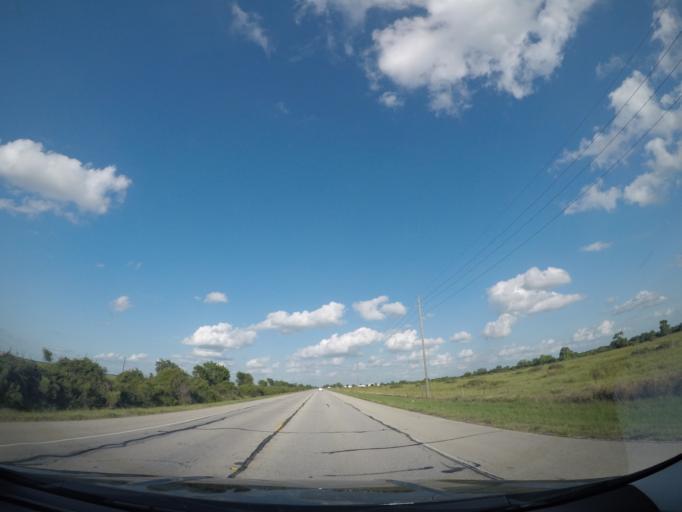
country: US
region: Texas
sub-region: Wharton County
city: East Bernard
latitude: 29.5466
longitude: -96.1817
